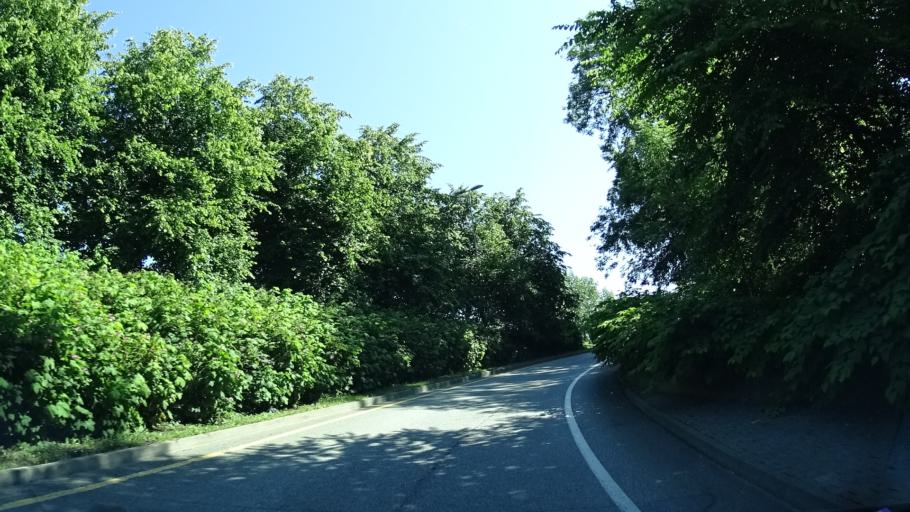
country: NO
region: Hordaland
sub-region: Bergen
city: Bergen
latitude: 60.3831
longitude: 5.3349
